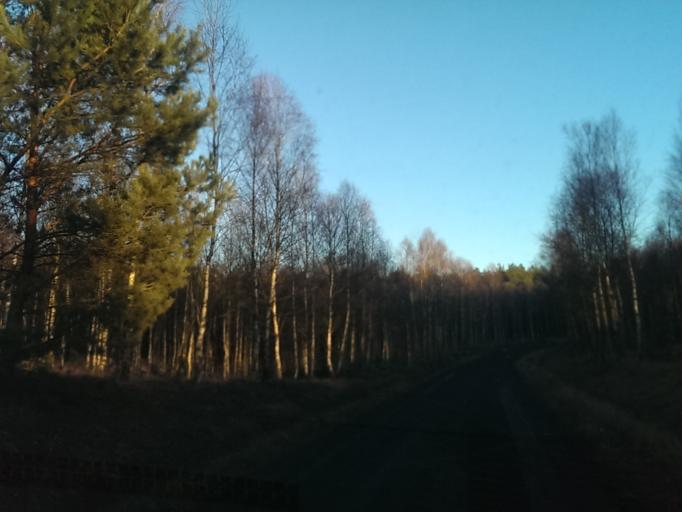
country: PL
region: Kujawsko-Pomorskie
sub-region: Powiat nakielski
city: Szubin
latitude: 53.0476
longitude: 17.6487
